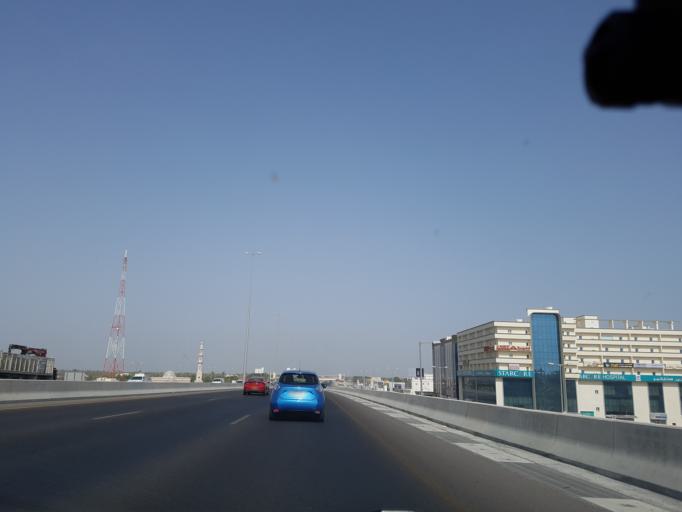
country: OM
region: Al Batinah
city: Barka'
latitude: 23.6676
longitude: 57.8824
